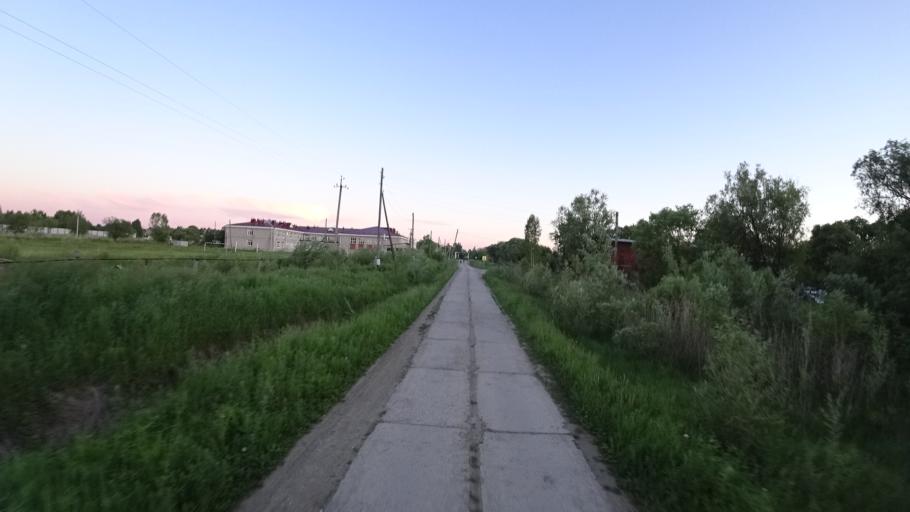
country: RU
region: Khabarovsk Krai
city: Khor
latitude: 47.8493
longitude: 134.9565
